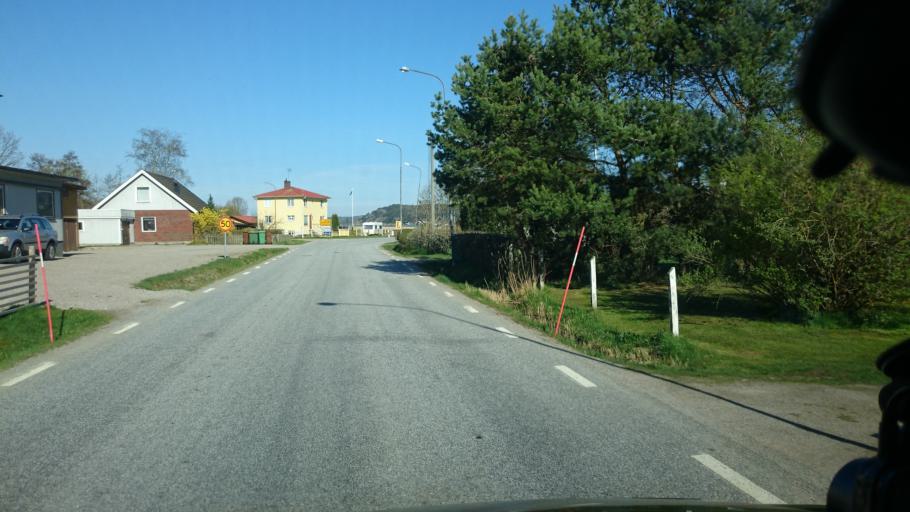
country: SE
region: Vaestra Goetaland
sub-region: Munkedals Kommun
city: Munkedal
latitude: 58.3803
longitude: 11.6679
